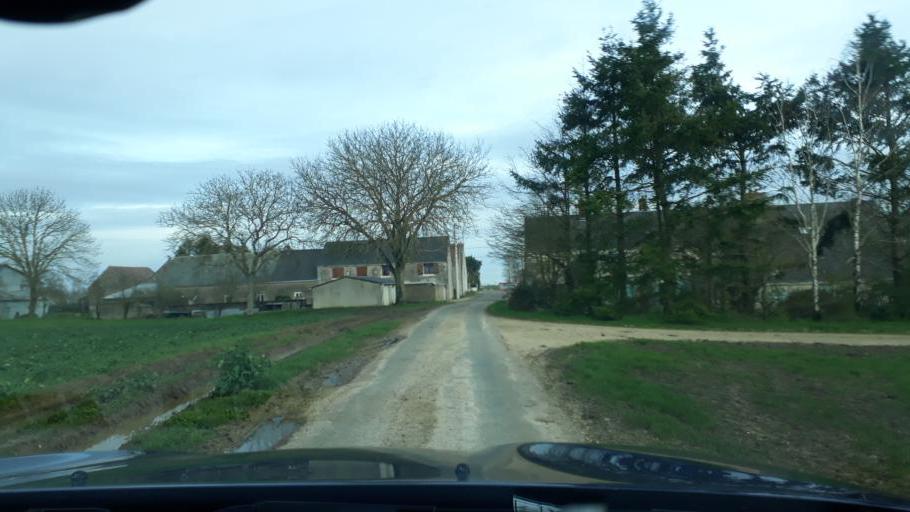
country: FR
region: Centre
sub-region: Departement du Loiret
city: Tavers
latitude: 47.7872
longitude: 1.5470
